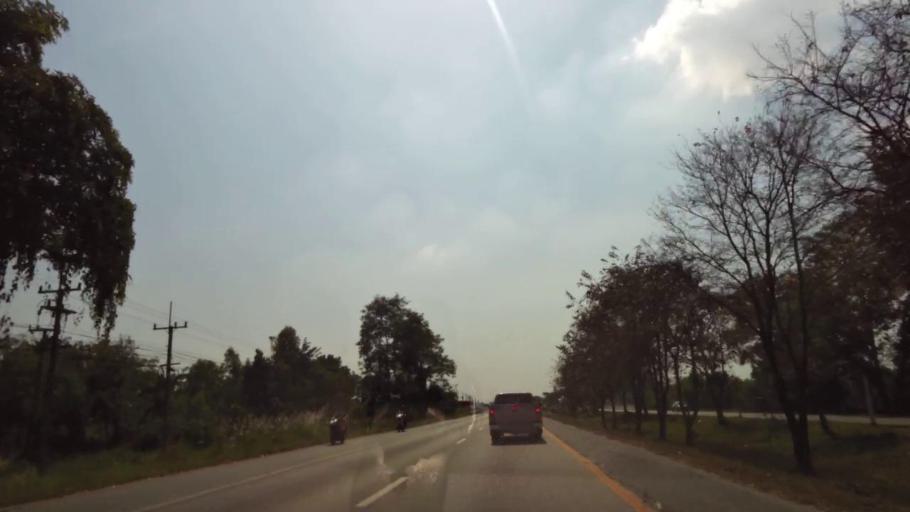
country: TH
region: Phichit
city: Wachira Barami
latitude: 16.5304
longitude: 100.1435
